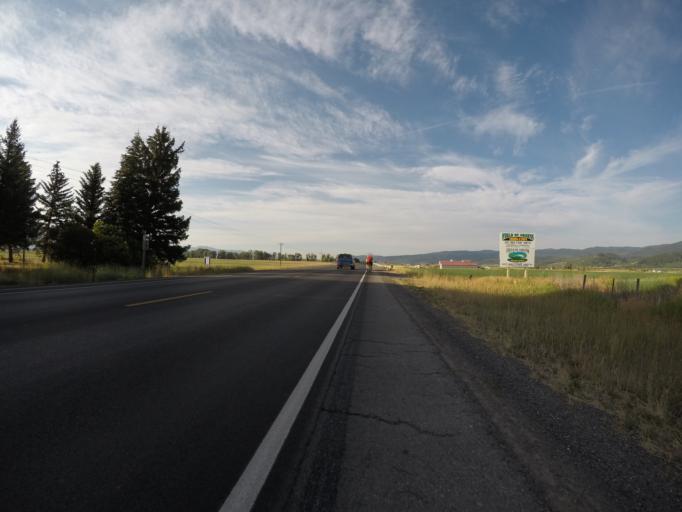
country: US
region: Wyoming
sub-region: Lincoln County
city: Afton
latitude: 42.9755
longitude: -111.0125
